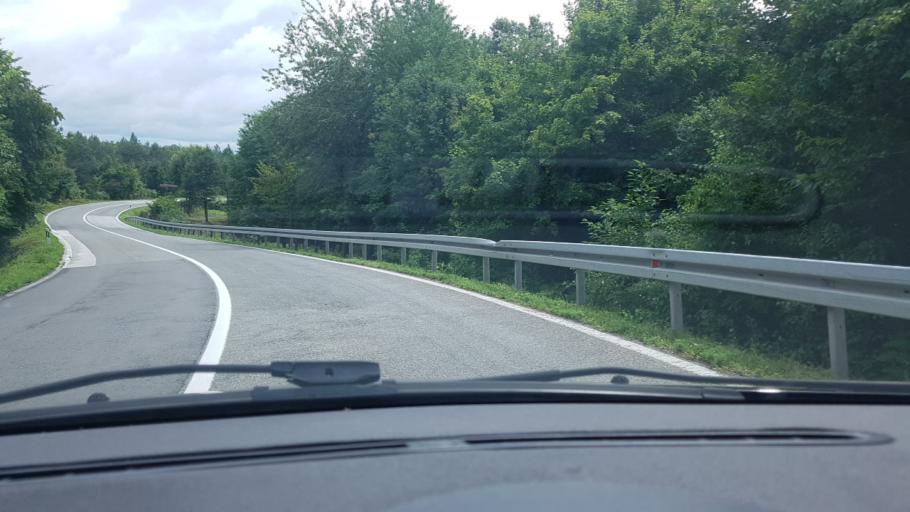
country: HR
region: Licko-Senjska
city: Jezerce
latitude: 44.9422
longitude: 15.6782
